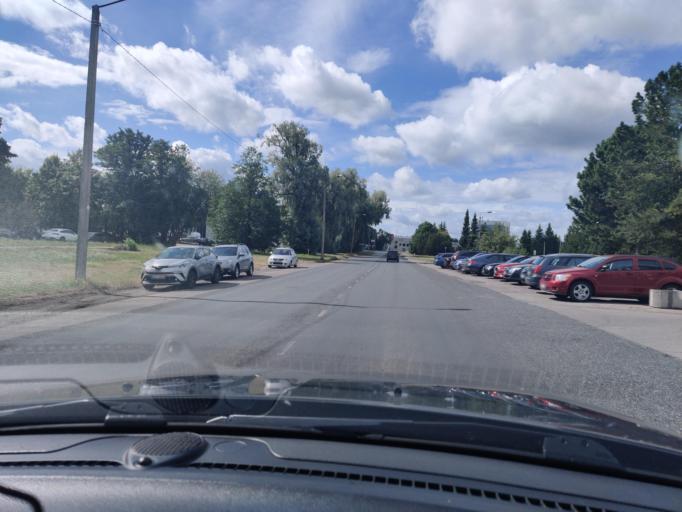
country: EE
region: Harju
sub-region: Tallinna linn
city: Tallinn
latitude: 59.4192
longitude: 24.6826
